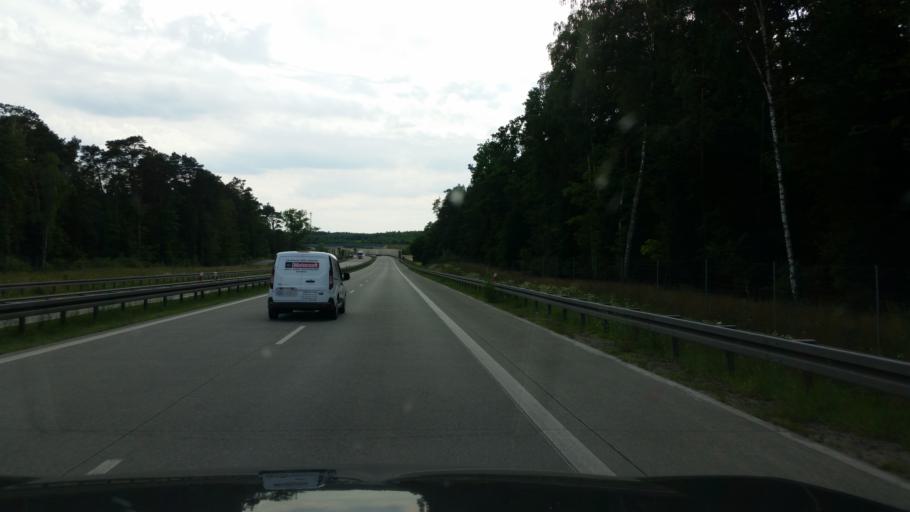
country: PL
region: Lodz Voivodeship
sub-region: Powiat rawski
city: Regnow
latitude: 51.8300
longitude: 20.3308
